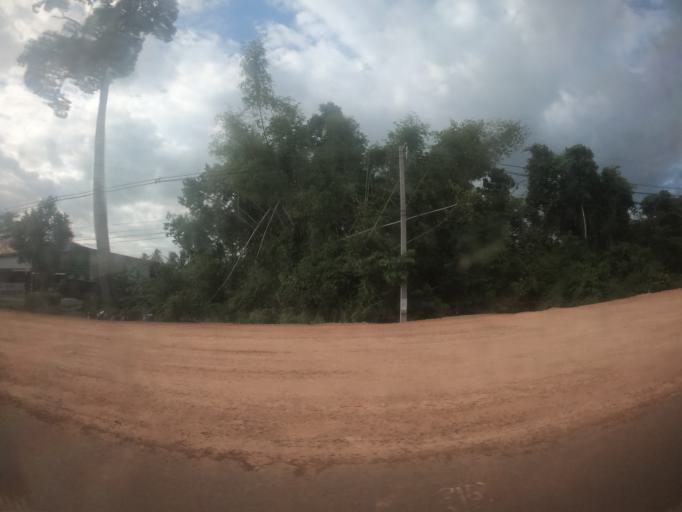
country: TH
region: Surin
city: Kap Choeng
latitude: 14.4720
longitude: 103.6110
